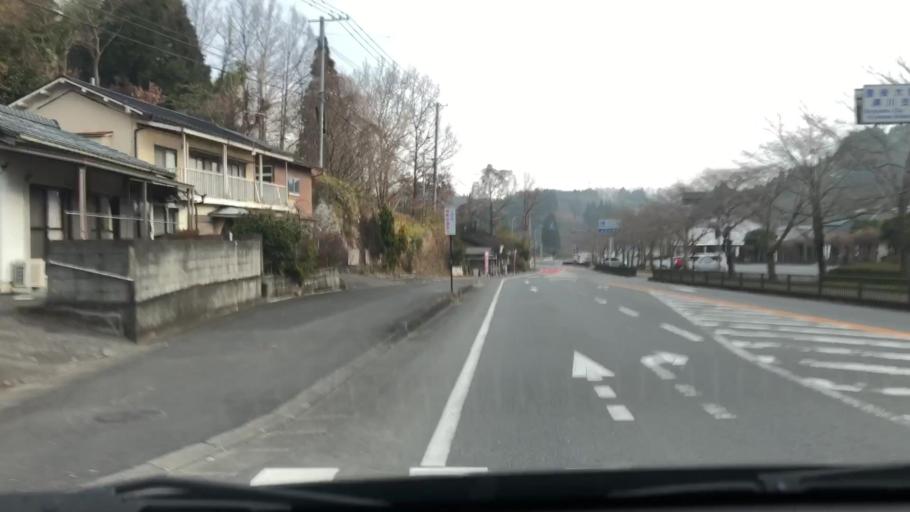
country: JP
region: Oita
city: Takedamachi
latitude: 32.9711
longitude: 131.5165
